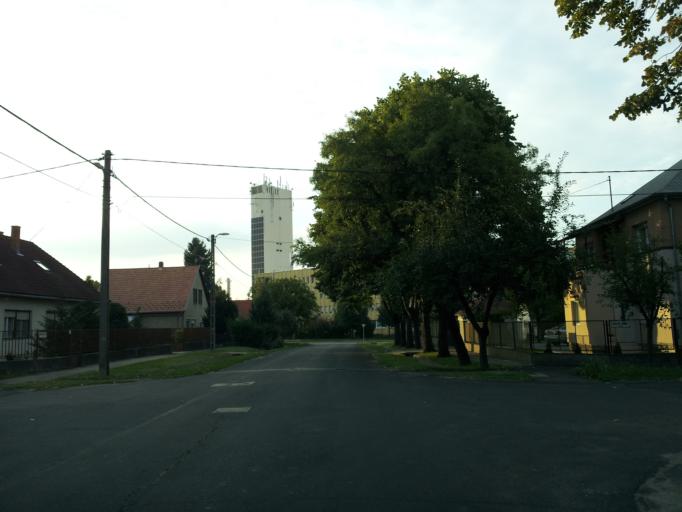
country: HU
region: Somogy
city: Siofok
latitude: 46.8991
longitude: 18.0441
